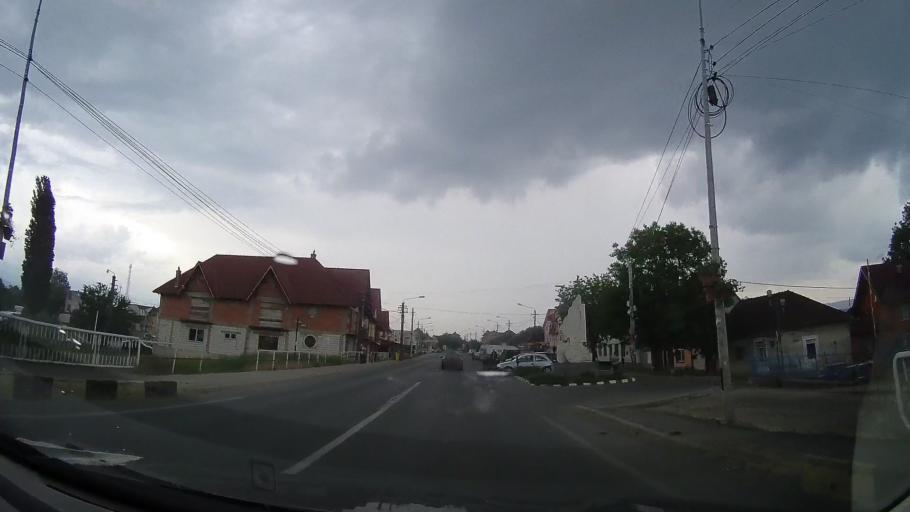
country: RO
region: Caras-Severin
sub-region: Municipiul Caransebes
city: Caransebes
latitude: 45.4076
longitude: 22.2225
